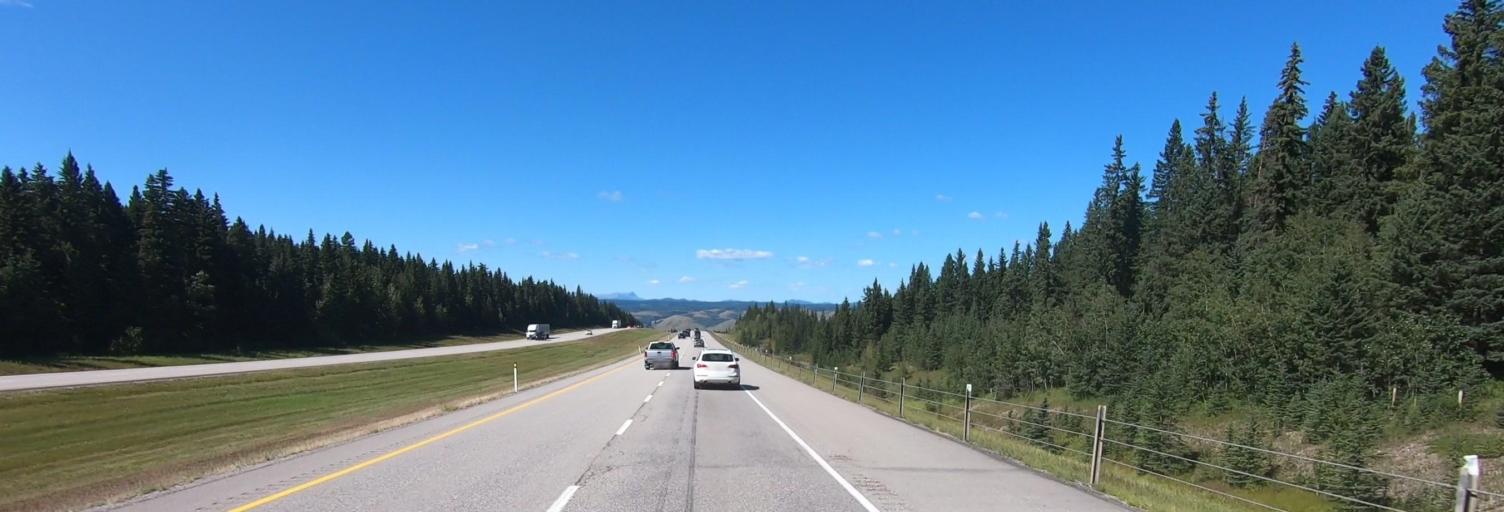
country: CA
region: Alberta
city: Cochrane
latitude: 51.1525
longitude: -114.7423
